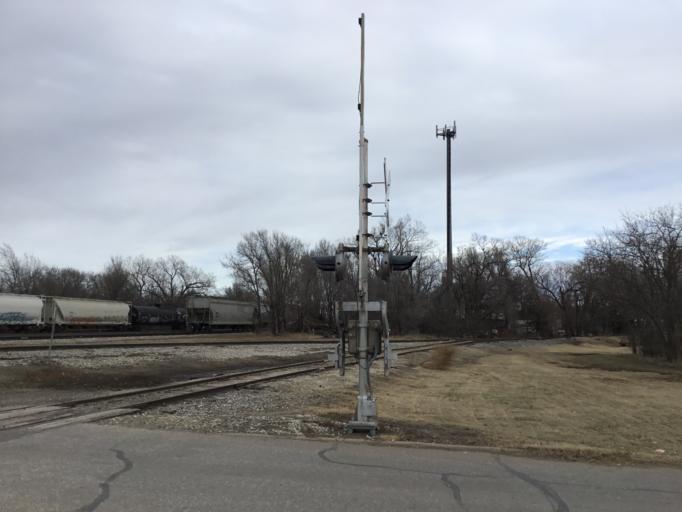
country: US
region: Kansas
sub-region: McPherson County
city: McPherson
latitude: 38.3722
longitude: -97.6761
